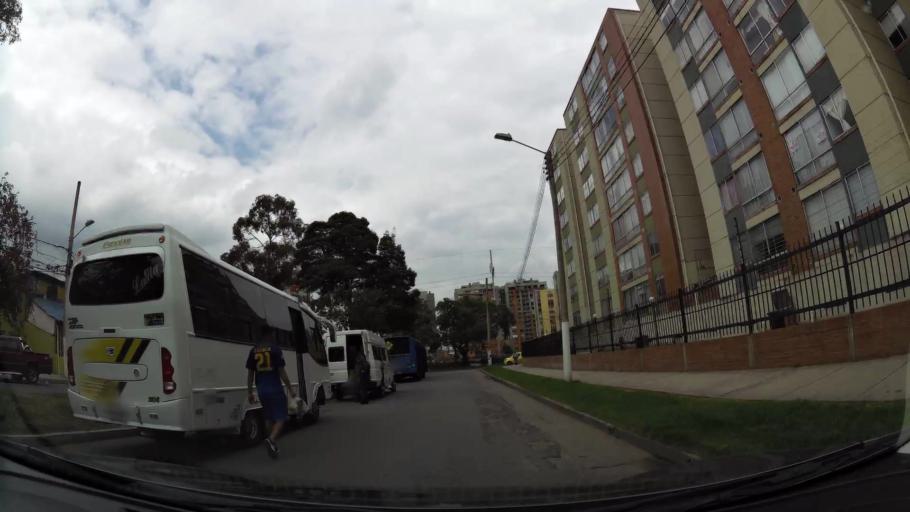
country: CO
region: Cundinamarca
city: La Calera
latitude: 4.7680
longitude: -74.0306
